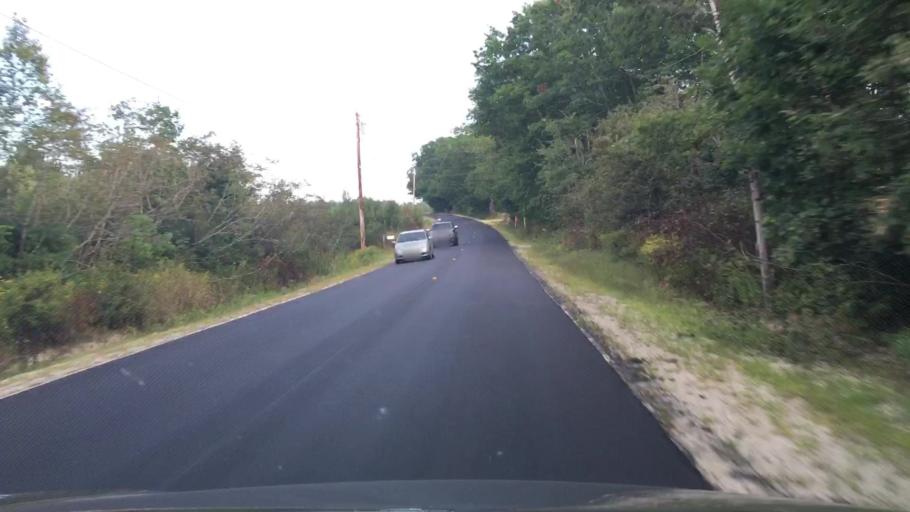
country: US
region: Maine
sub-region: Hancock County
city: Penobscot
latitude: 44.5389
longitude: -68.6156
